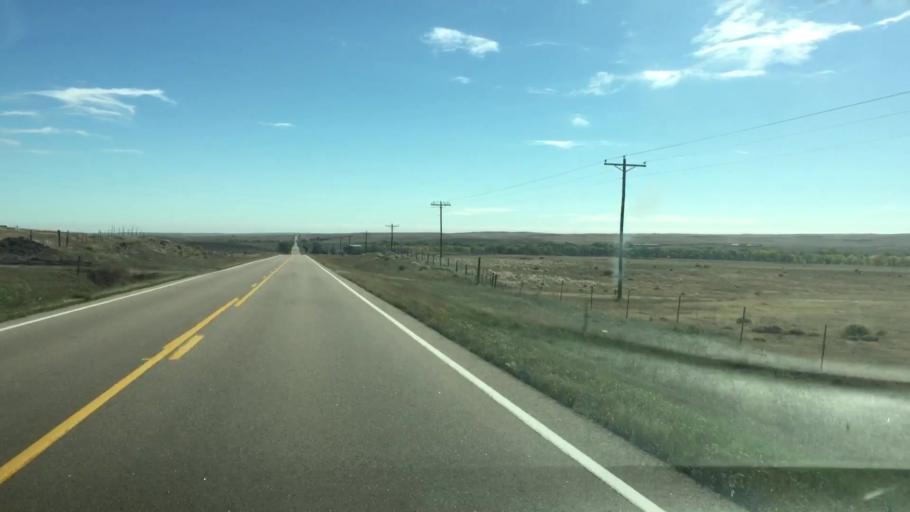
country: US
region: Colorado
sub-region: Elbert County
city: Kiowa
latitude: 39.2735
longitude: -104.1685
